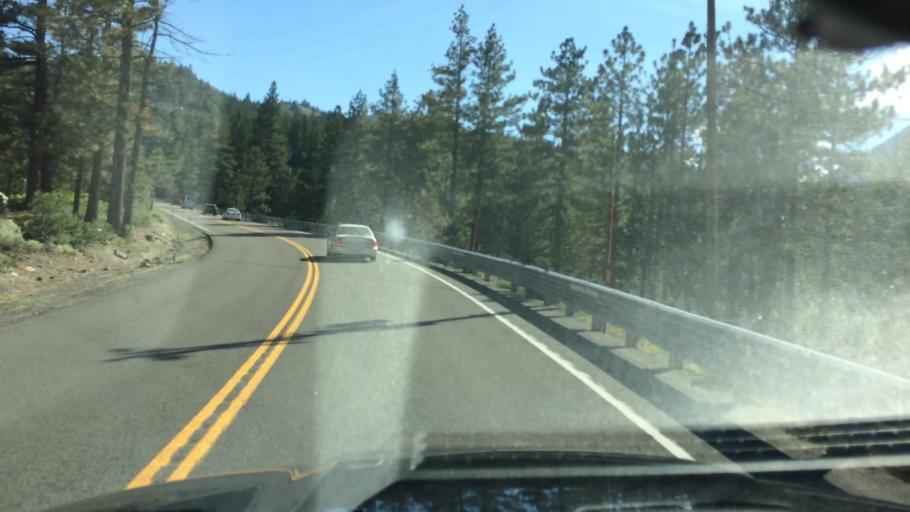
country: US
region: Nevada
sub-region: Washoe County
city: Incline Village
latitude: 39.3443
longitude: -119.8634
